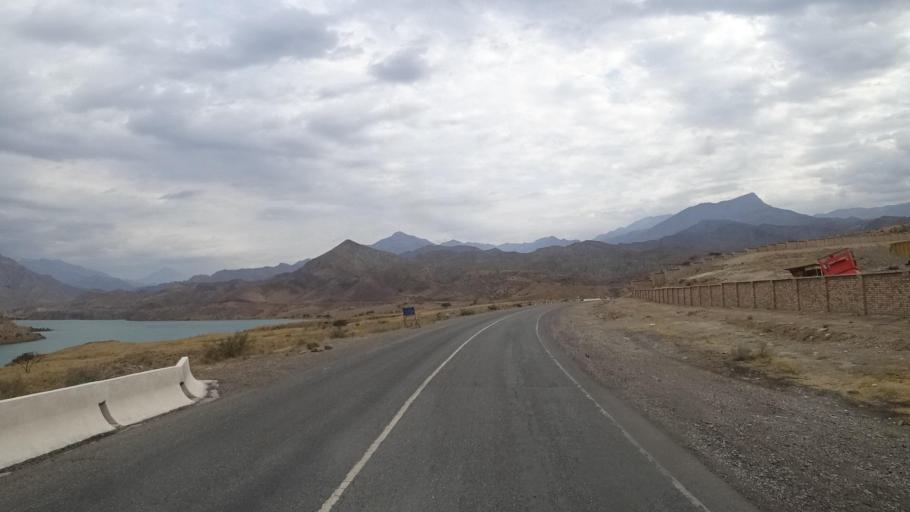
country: KG
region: Jalal-Abad
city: Tash-Kumyr
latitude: 41.4210
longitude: 72.2426
